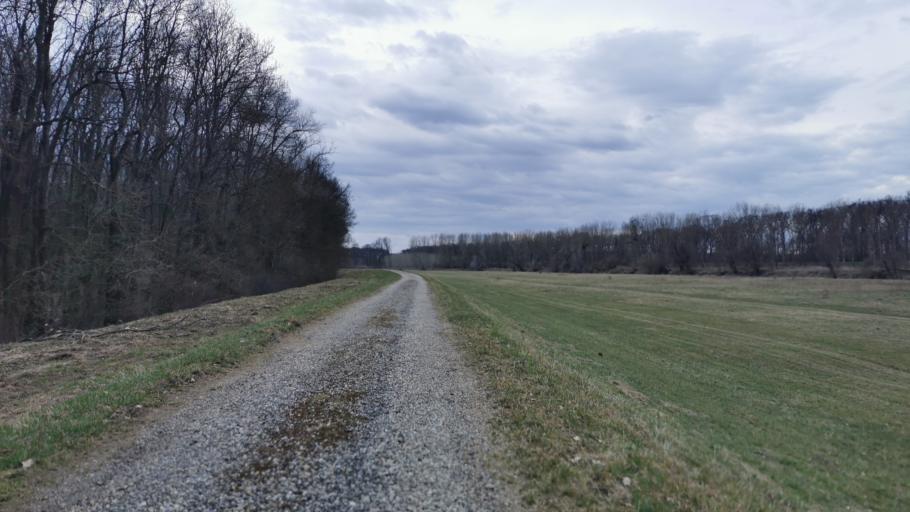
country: CZ
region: South Moravian
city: Hodonin
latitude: 48.8271
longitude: 17.1088
